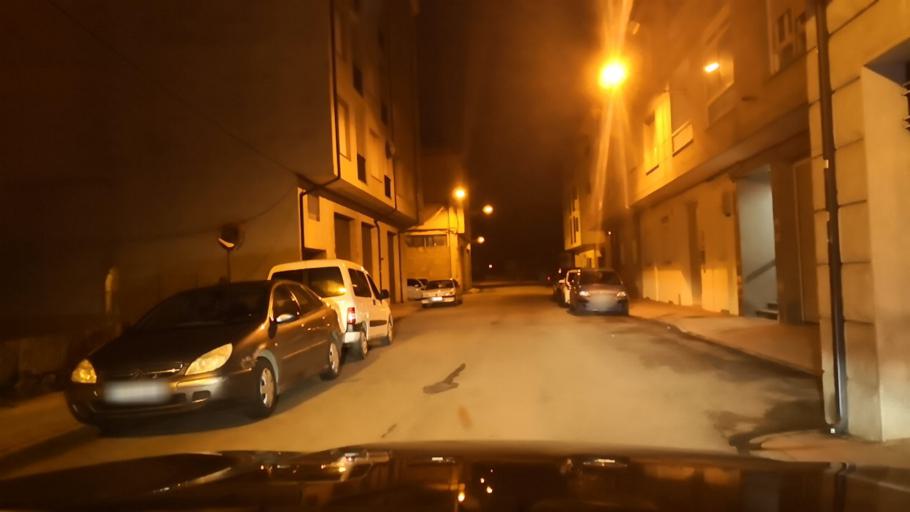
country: ES
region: Galicia
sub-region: Provincia de Ourense
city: Verin
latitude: 41.9402
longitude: -7.4297
